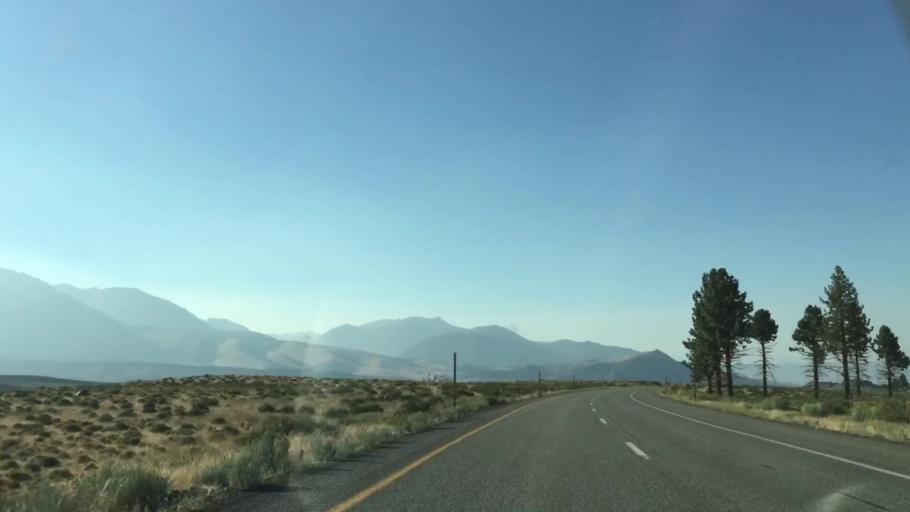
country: US
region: California
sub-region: Mono County
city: Mammoth Lakes
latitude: 37.8306
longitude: -119.0679
